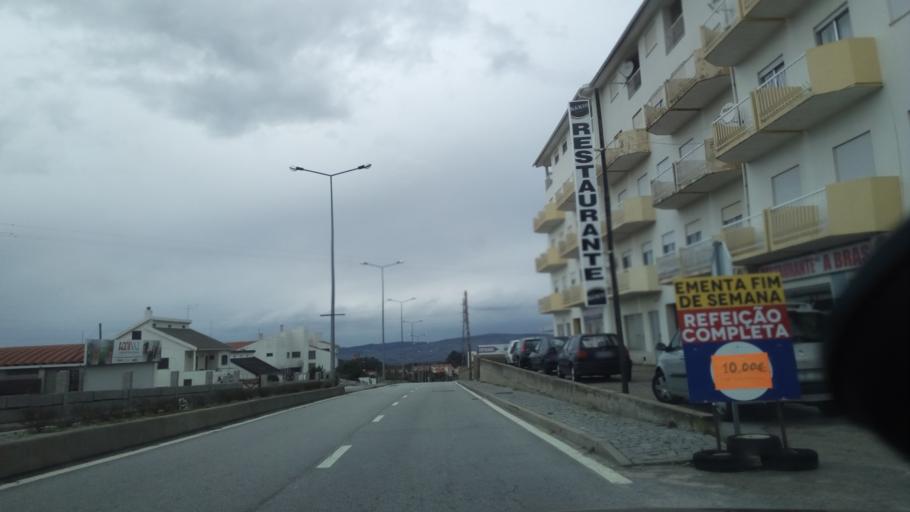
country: PT
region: Guarda
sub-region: Manteigas
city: Manteigas
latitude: 40.4947
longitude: -7.6014
